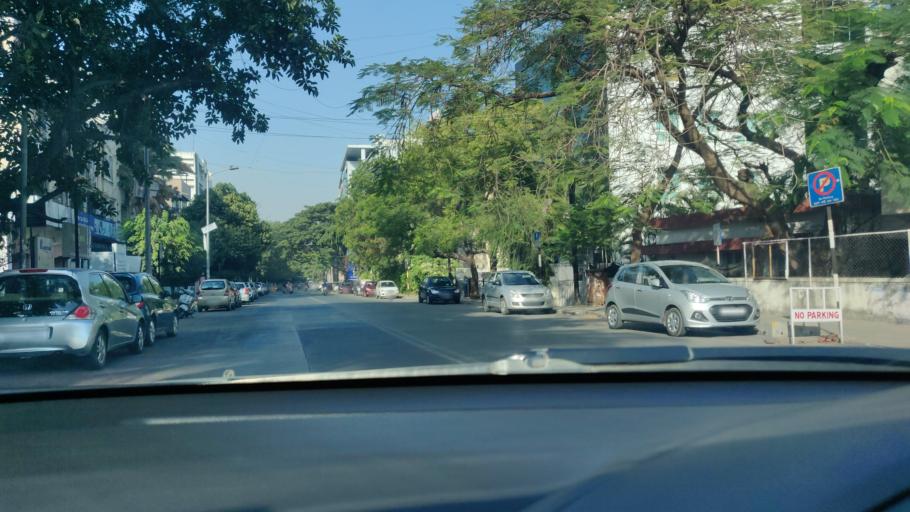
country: IN
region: Maharashtra
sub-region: Pune Division
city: Khadki
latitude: 18.5533
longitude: 73.8094
